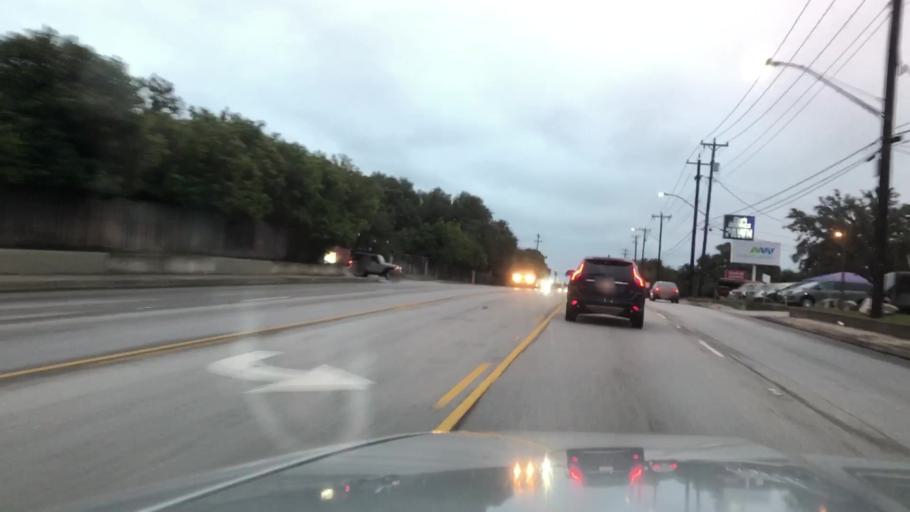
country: US
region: Texas
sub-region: Bexar County
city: Leon Valley
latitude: 29.5583
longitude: -98.6151
